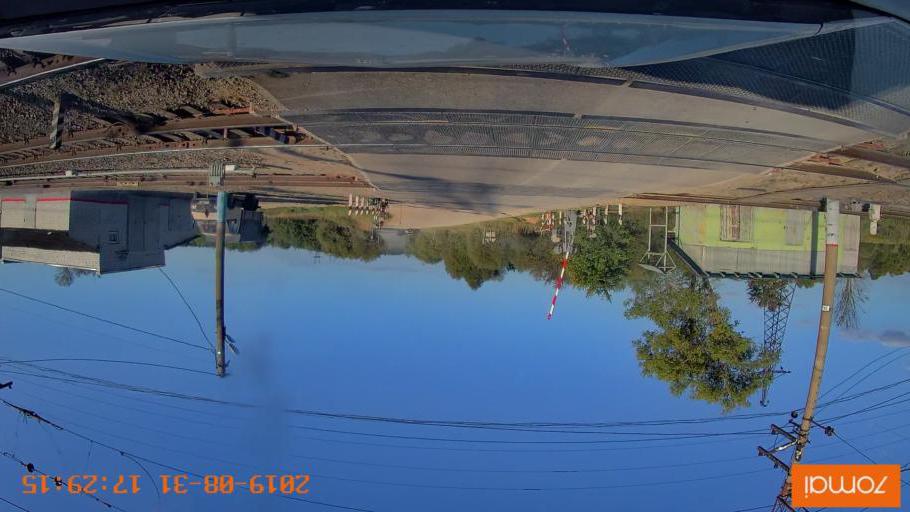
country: RU
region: Kaluga
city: Detchino
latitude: 54.8135
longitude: 36.3247
